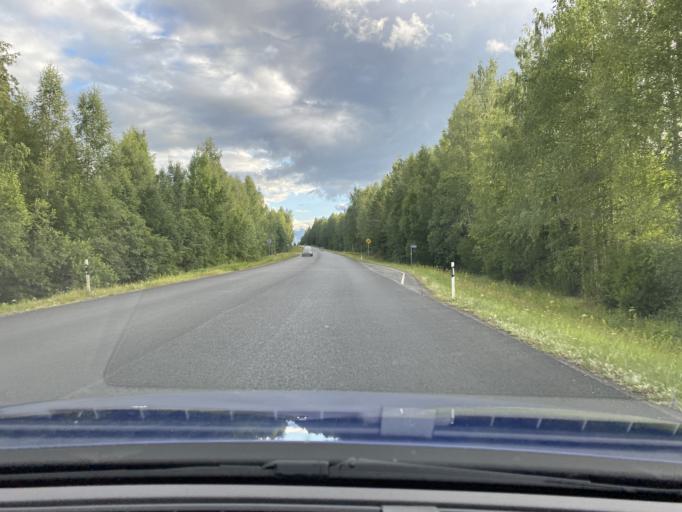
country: FI
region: Haeme
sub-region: Haemeenlinna
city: Renko
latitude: 60.9239
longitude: 24.3403
